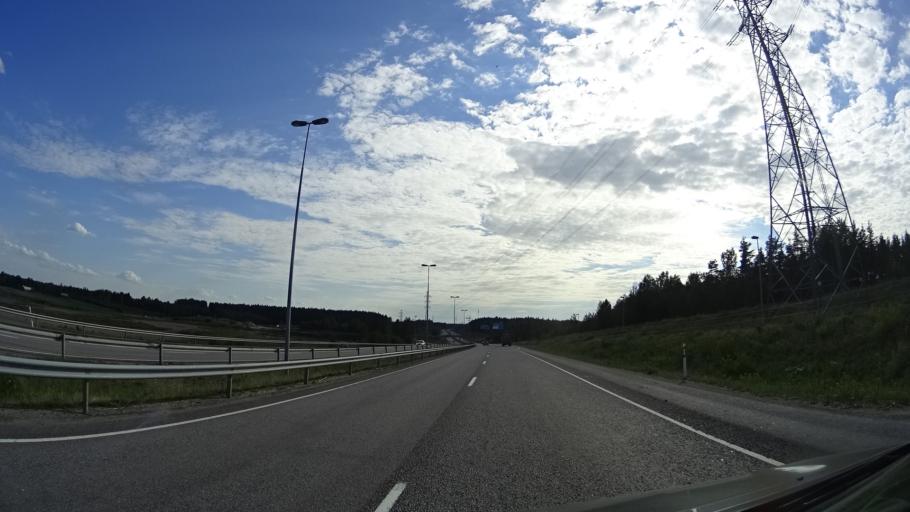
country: FI
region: South Karelia
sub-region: Lappeenranta
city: Lappeenranta
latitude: 61.0693
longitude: 28.3006
